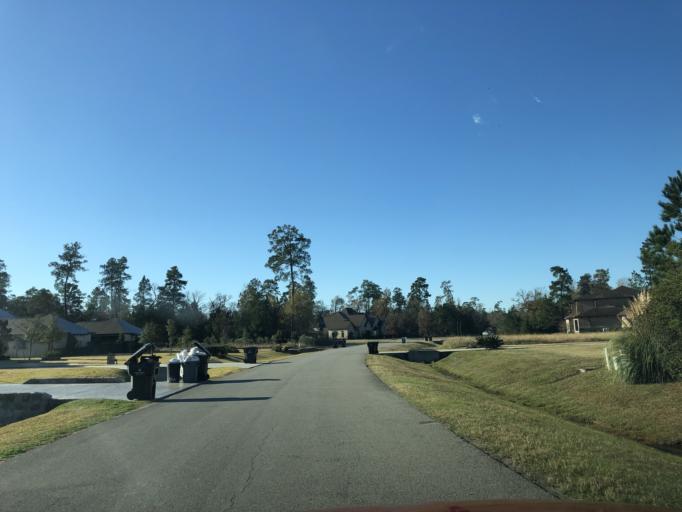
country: US
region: Texas
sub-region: Montgomery County
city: Porter Heights
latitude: 30.0722
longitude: -95.3186
